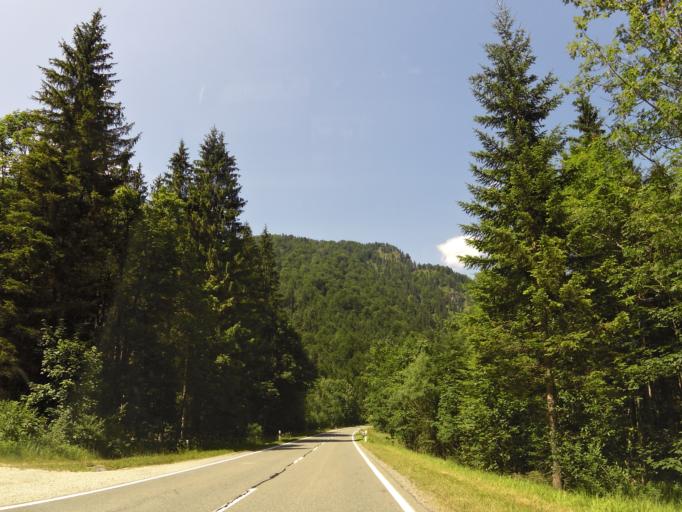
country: DE
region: Bavaria
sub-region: Upper Bavaria
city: Reit im Winkl
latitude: 47.6753
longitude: 12.5466
